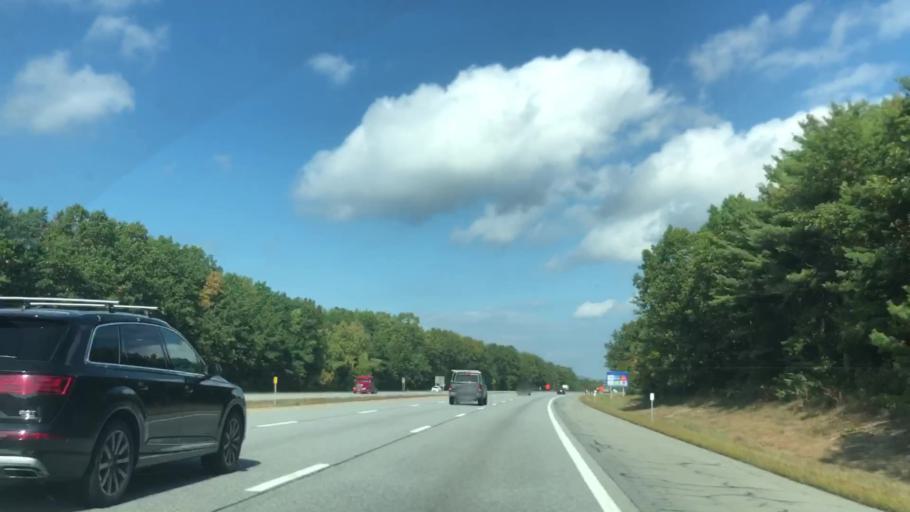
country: US
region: New York
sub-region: Warren County
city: West Glens Falls
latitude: 43.2891
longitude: -73.6810
